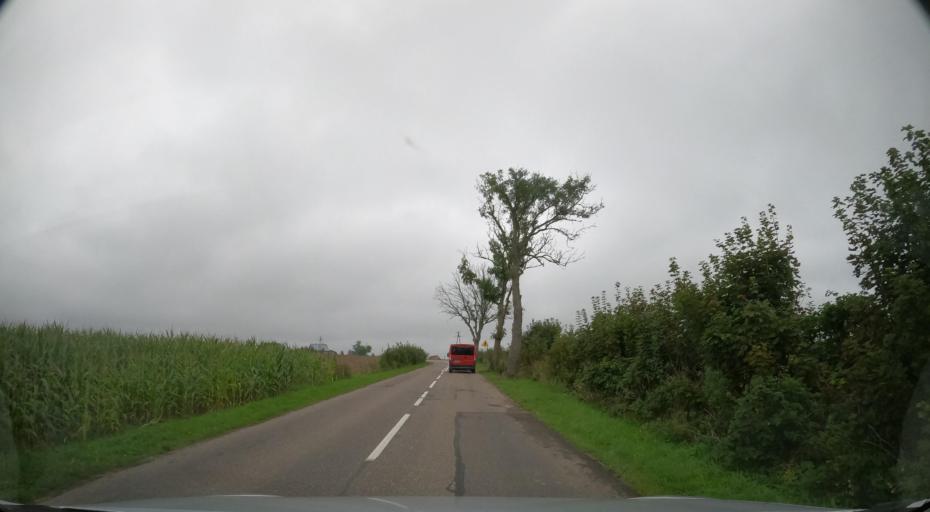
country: PL
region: Pomeranian Voivodeship
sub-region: Powiat wejherowski
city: Luzino
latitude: 54.4963
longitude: 18.1414
